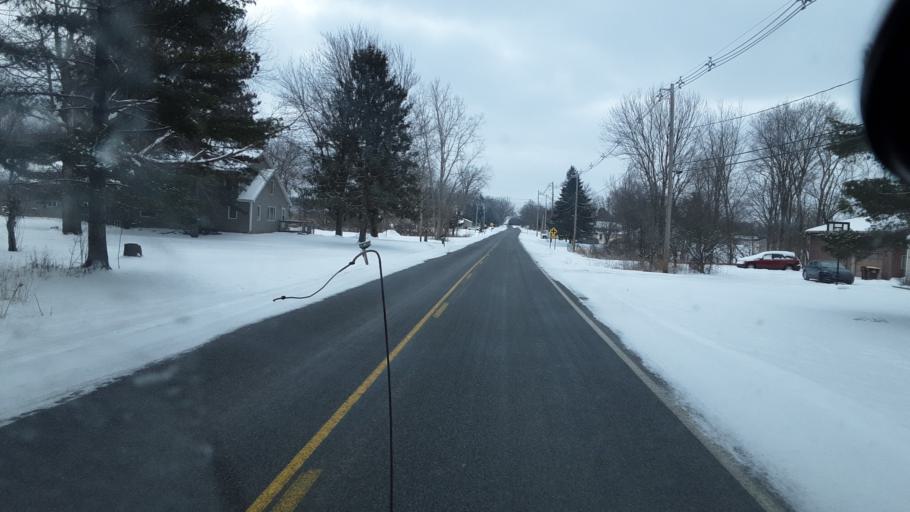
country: US
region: Michigan
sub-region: Ingham County
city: Holt
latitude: 42.5992
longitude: -84.5428
